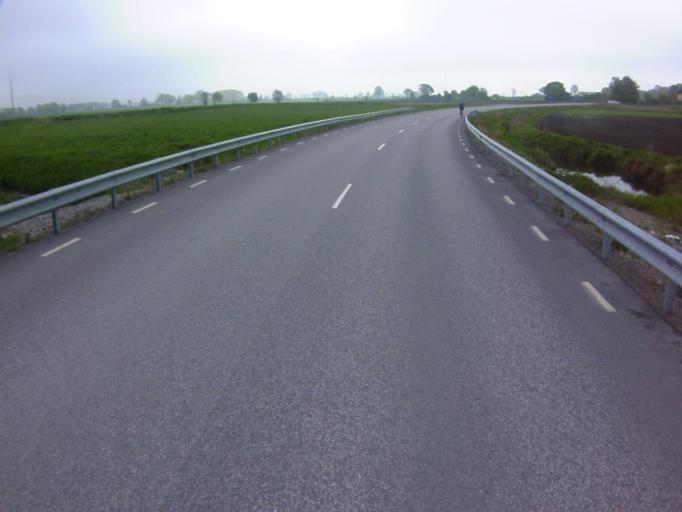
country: SE
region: Blekinge
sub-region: Solvesborgs Kommun
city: Soelvesborg
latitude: 56.0437
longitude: 14.6200
